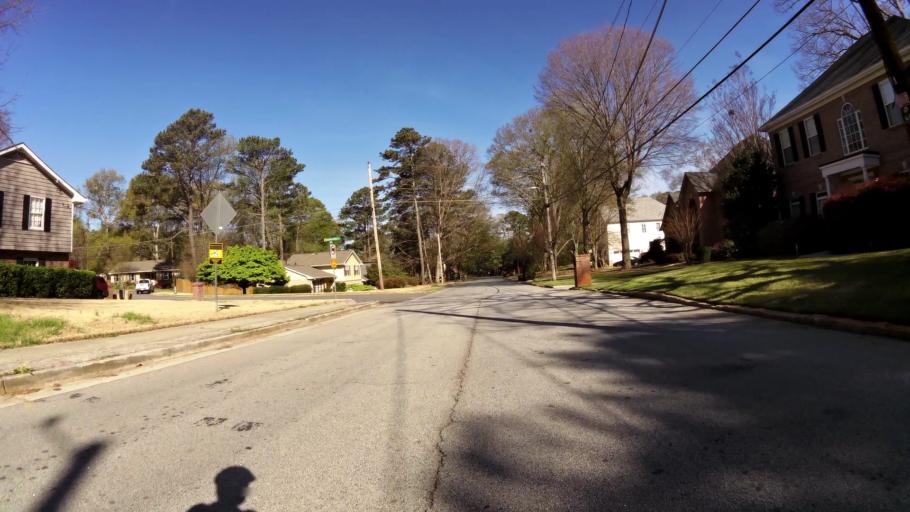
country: US
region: Georgia
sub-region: DeKalb County
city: Clarkston
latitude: 33.8256
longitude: -84.2650
